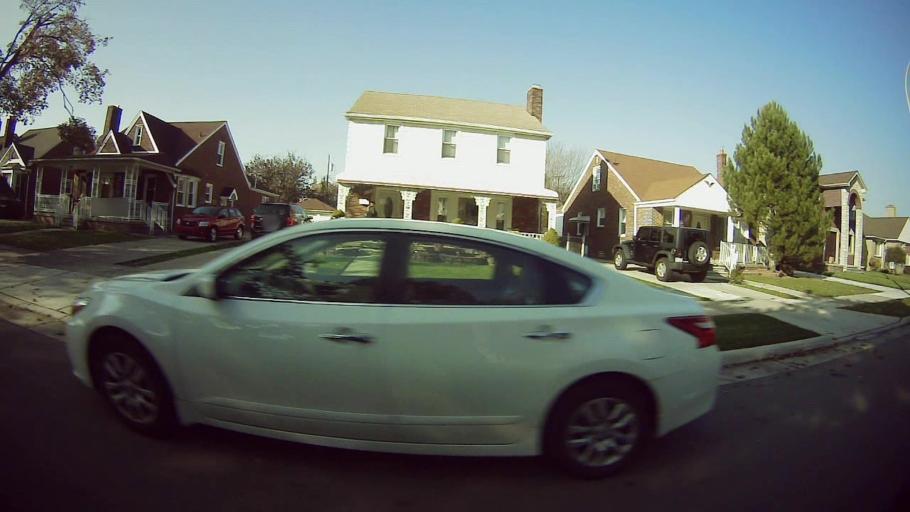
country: US
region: Michigan
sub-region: Wayne County
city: Dearborn
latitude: 42.3334
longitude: -83.1692
